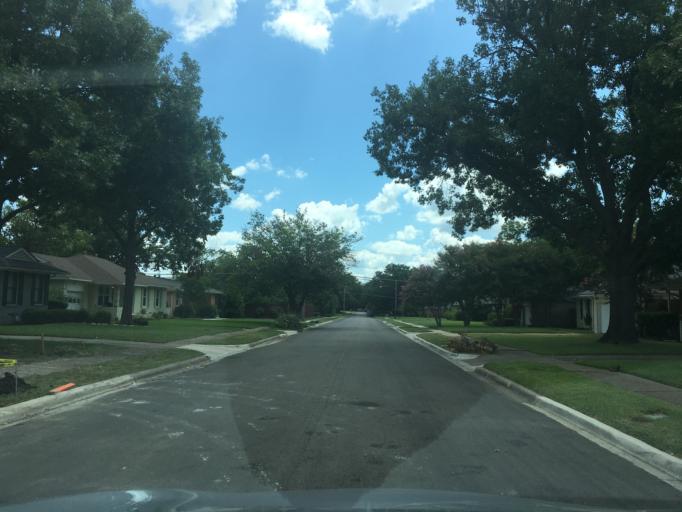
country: US
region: Texas
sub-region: Dallas County
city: Richardson
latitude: 32.8683
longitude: -96.7091
